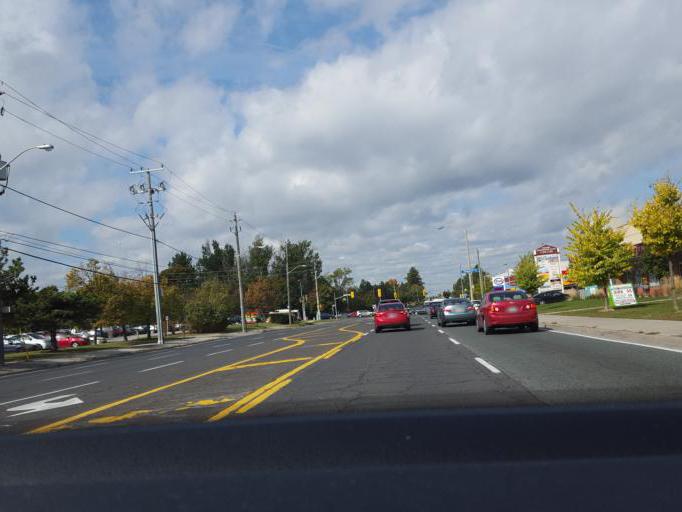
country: CA
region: Ontario
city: Scarborough
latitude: 43.8005
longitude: -79.1991
